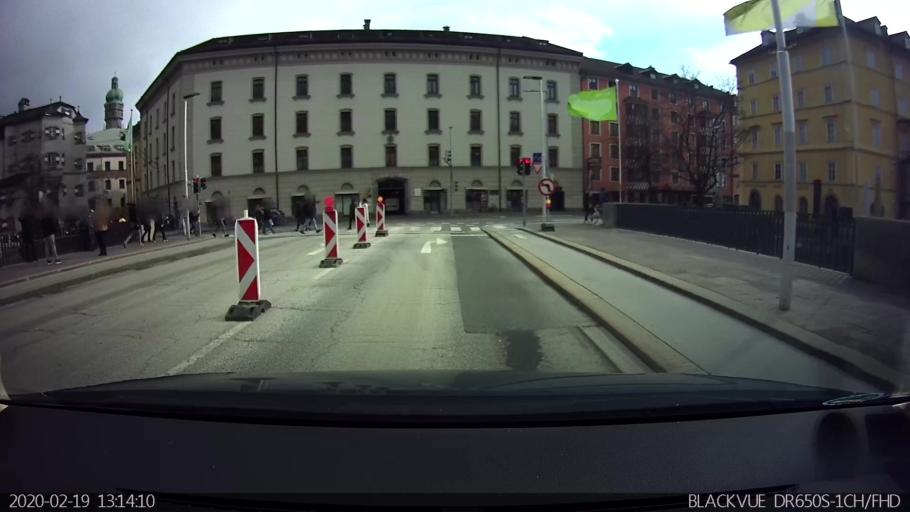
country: AT
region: Tyrol
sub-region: Innsbruck Stadt
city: Innsbruck
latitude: 47.2689
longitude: 11.3911
